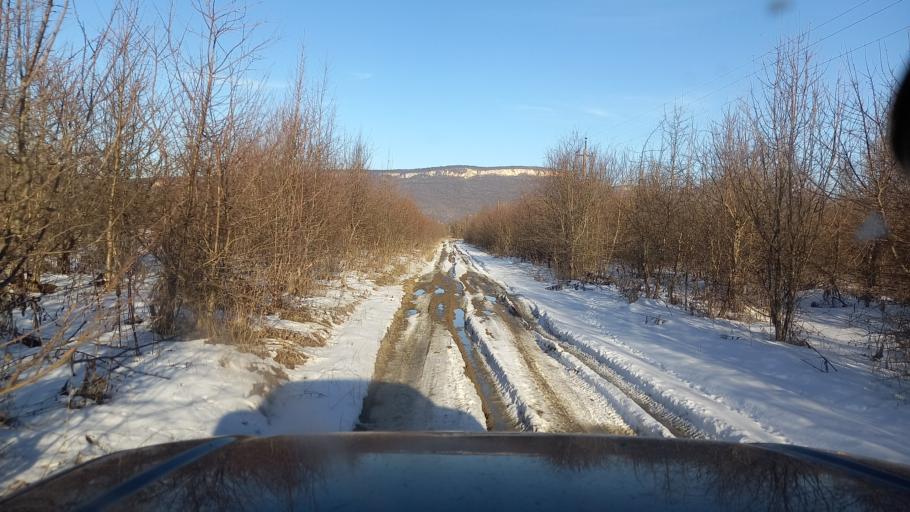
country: RU
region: Adygeya
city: Kamennomostskiy
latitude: 44.2137
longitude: 40.1701
